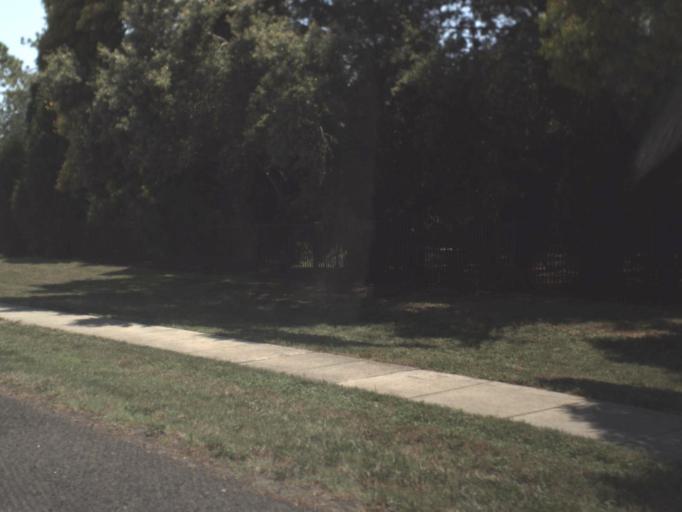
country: US
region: Florida
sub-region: Pinellas County
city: Palm Harbor
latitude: 28.1058
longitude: -82.7400
